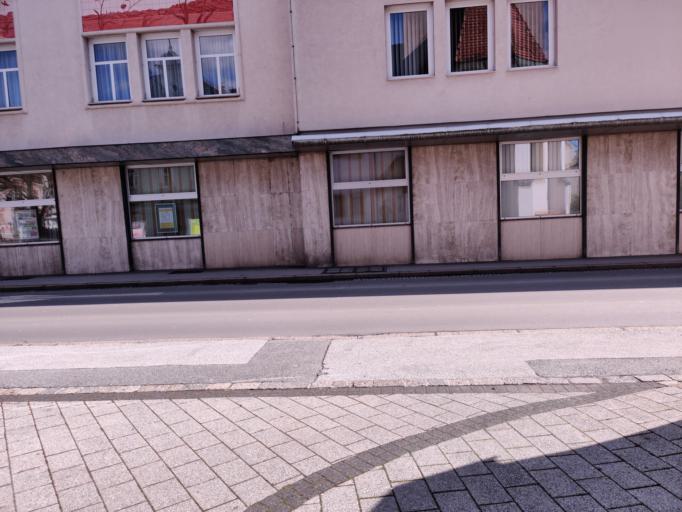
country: AT
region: Styria
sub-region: Politischer Bezirk Voitsberg
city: Voitsberg
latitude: 47.0492
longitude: 15.1498
